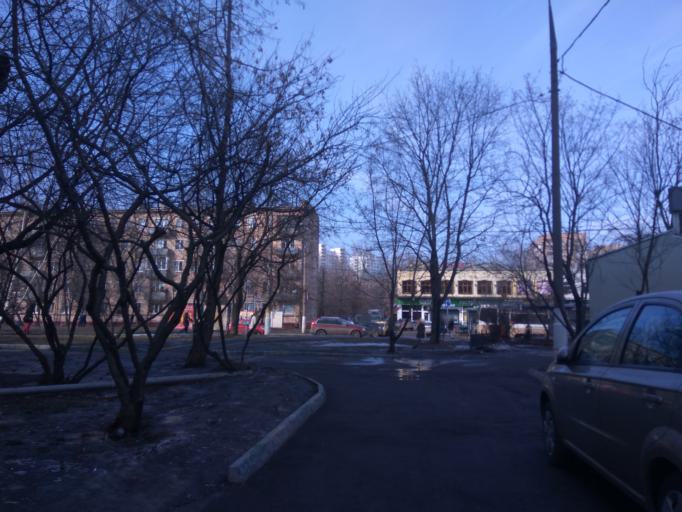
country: RU
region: Moscow
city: Kolomenskoye
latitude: 55.6824
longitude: 37.6813
